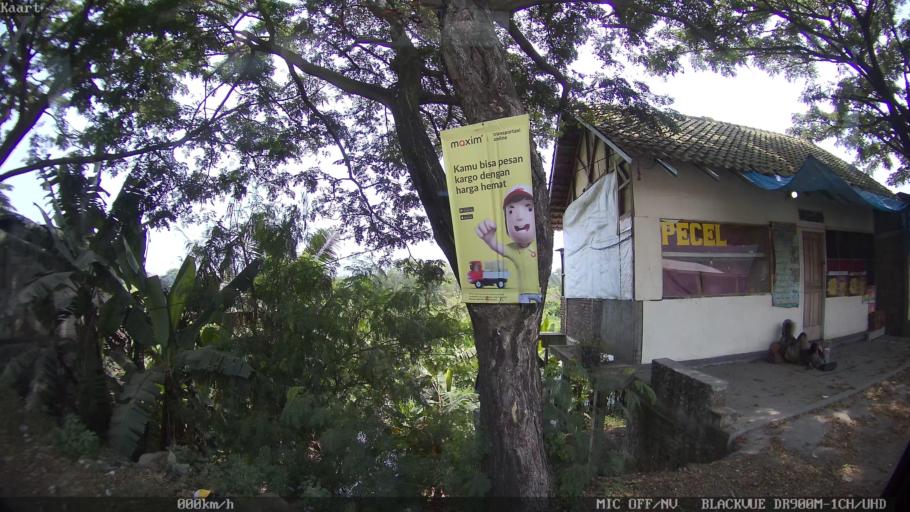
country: ID
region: Banten
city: Curug
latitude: -5.9573
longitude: 106.0047
